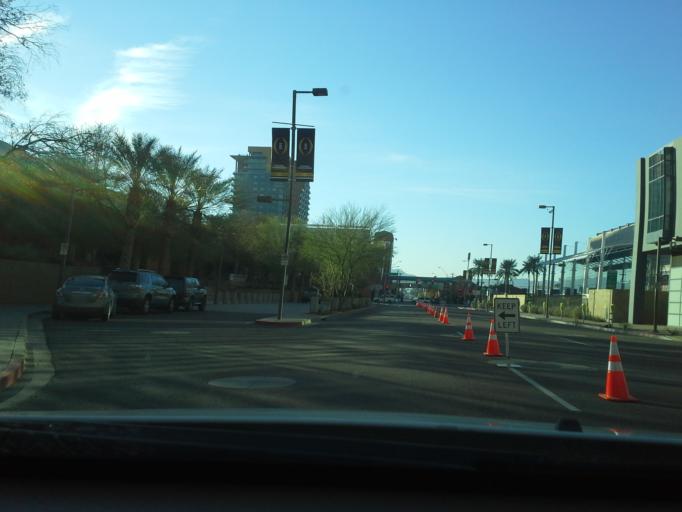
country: US
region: Arizona
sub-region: Maricopa County
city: Phoenix
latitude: 33.4480
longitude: -112.0700
